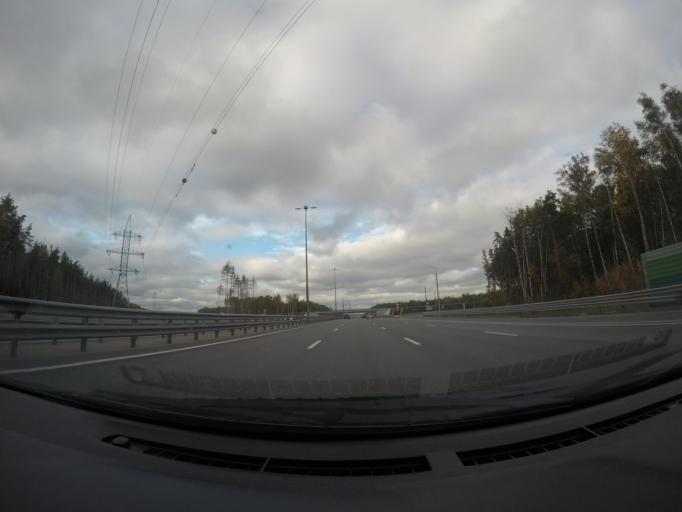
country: RU
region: Moskovskaya
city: Odintsovo
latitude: 55.7091
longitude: 37.3113
